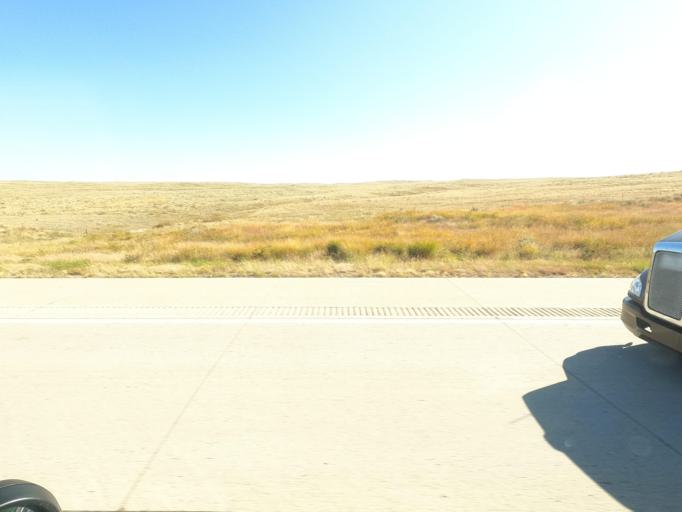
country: US
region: Nebraska
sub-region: Deuel County
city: Chappell
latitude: 40.9231
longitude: -102.4520
